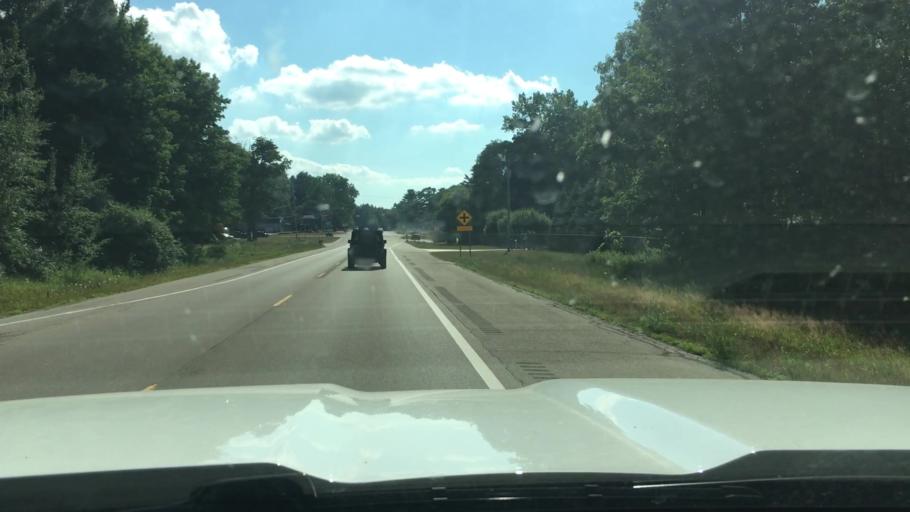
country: US
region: Michigan
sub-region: Kent County
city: Rockford
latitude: 43.0857
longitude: -85.4475
